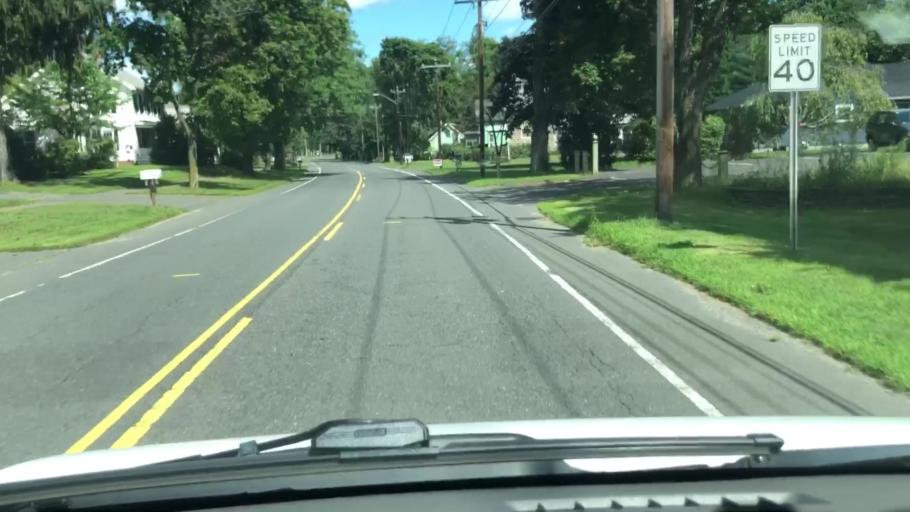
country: US
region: Massachusetts
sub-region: Hampshire County
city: Hatfield
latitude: 42.3624
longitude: -72.6143
